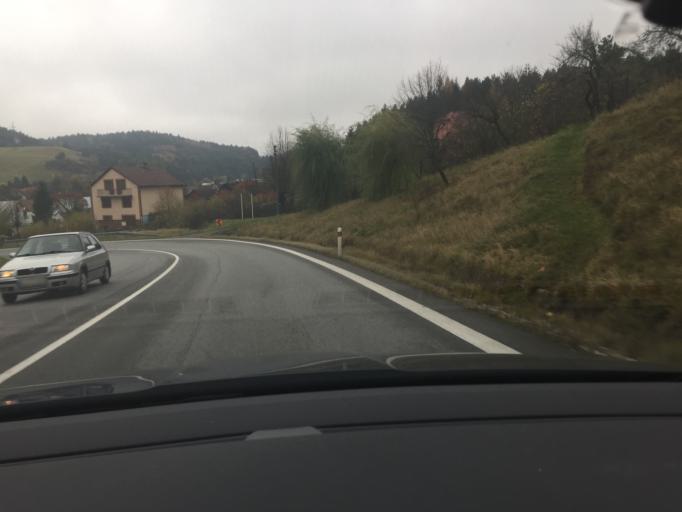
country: SK
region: Presovsky
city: Stara L'ubovna
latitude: 49.2673
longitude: 20.7714
